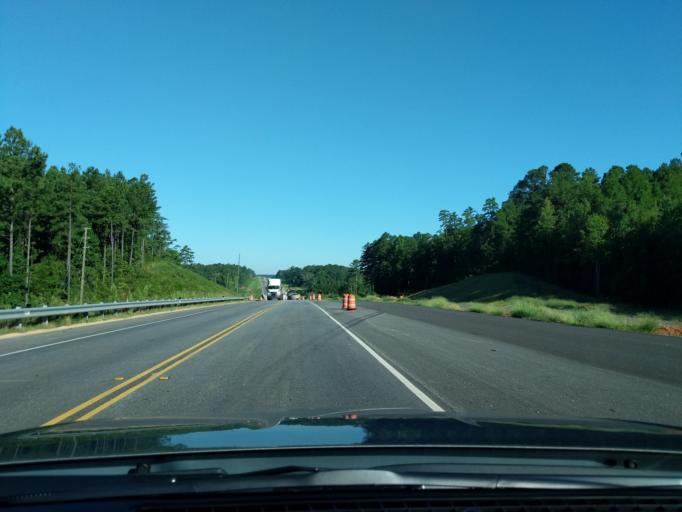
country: US
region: Georgia
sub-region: McDuffie County
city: Thomson
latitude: 33.5787
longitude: -82.5267
